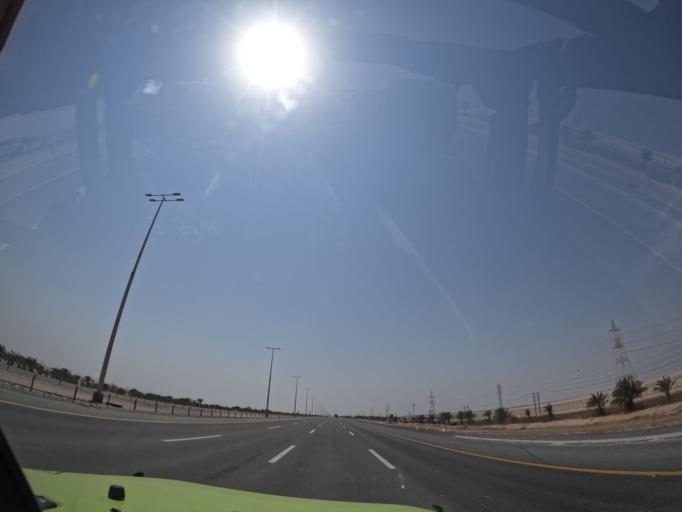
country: AE
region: Abu Dhabi
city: Abu Dhabi
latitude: 24.2016
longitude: 54.3984
